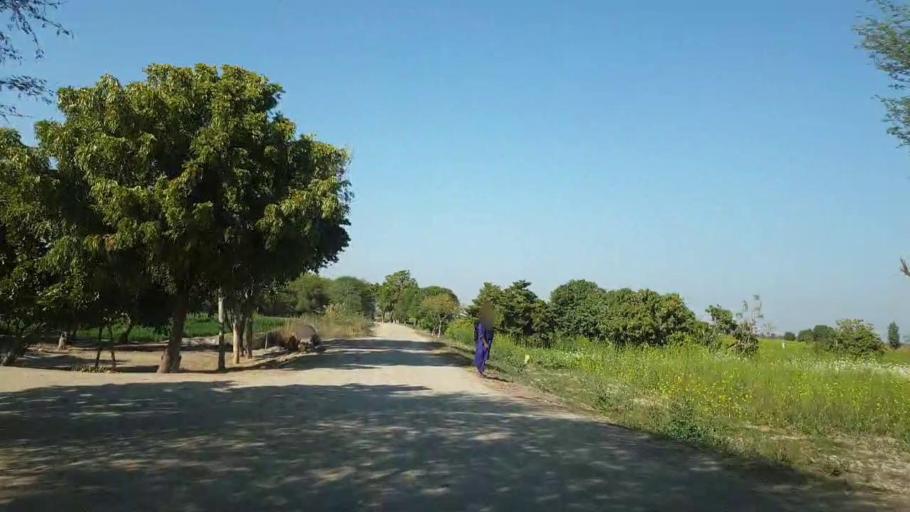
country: PK
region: Sindh
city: Mirpur Khas
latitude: 25.6480
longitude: 69.0493
